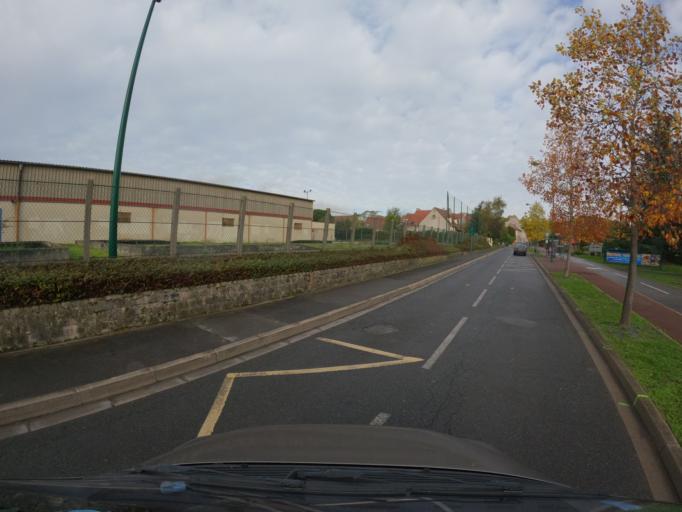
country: FR
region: Ile-de-France
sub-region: Departement de Seine-et-Marne
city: Courtry
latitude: 48.9157
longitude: 2.6037
